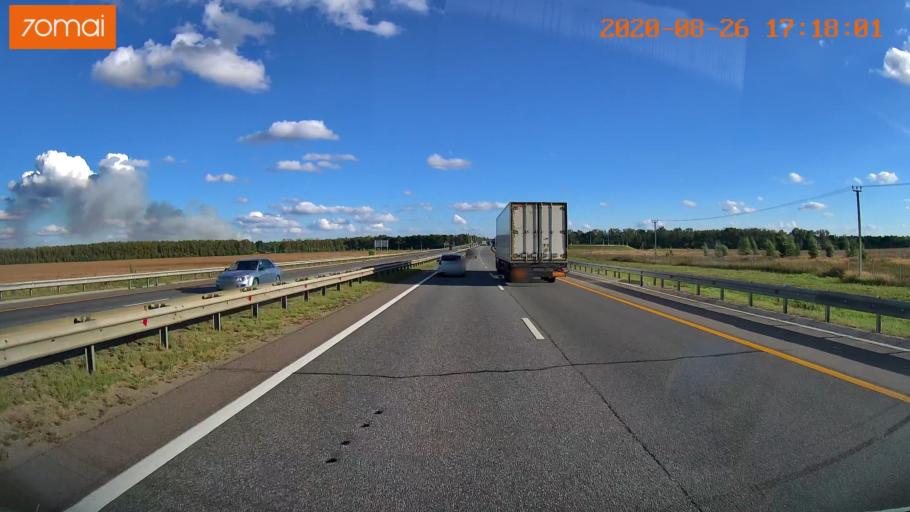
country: RU
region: Tula
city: Volovo
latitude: 53.6154
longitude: 38.0929
